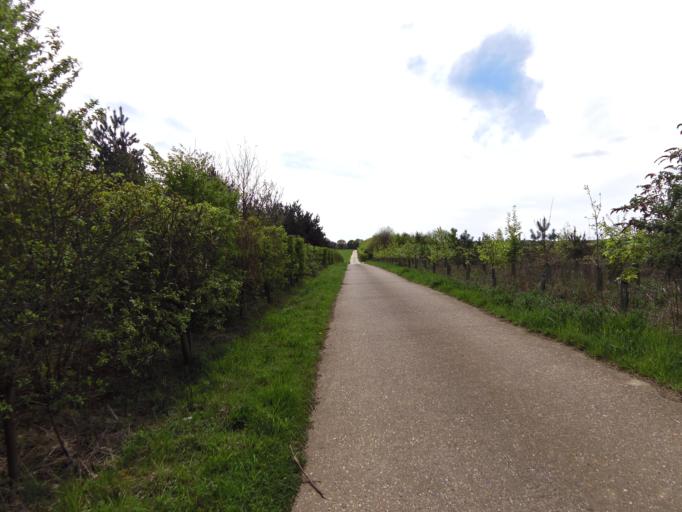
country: GB
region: England
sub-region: Suffolk
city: Ipswich
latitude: 52.0155
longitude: 1.1389
